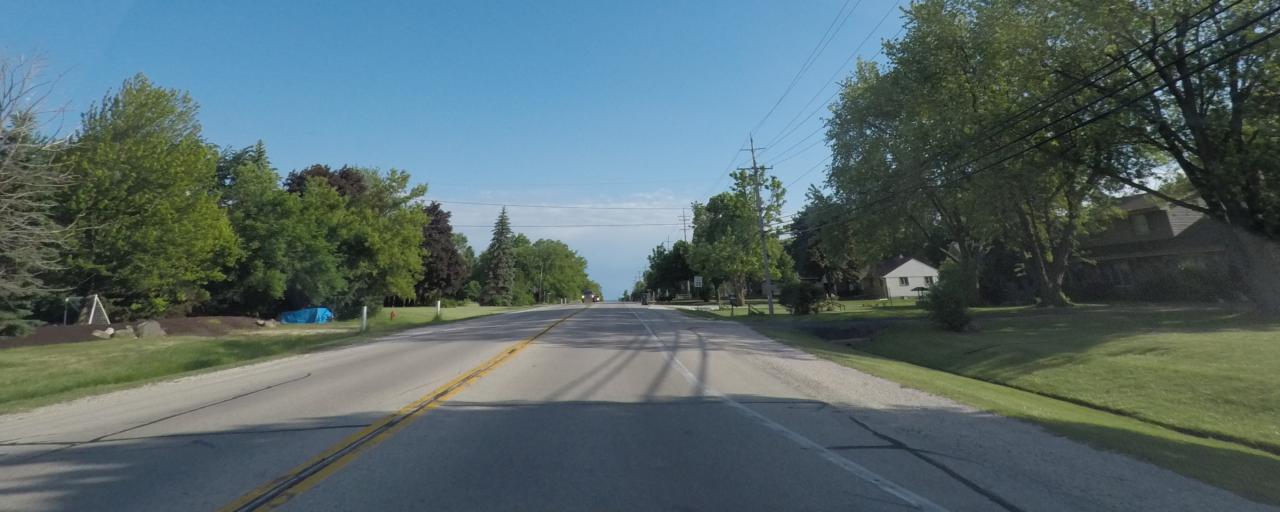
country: US
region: Wisconsin
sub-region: Waukesha County
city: New Berlin
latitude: 42.9503
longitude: -88.0893
